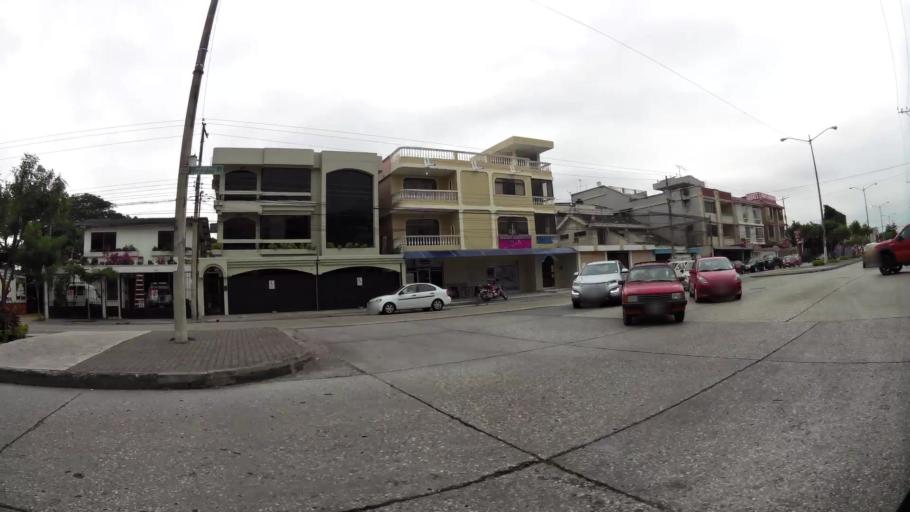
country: EC
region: Guayas
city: Eloy Alfaro
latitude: -2.1512
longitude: -79.8903
